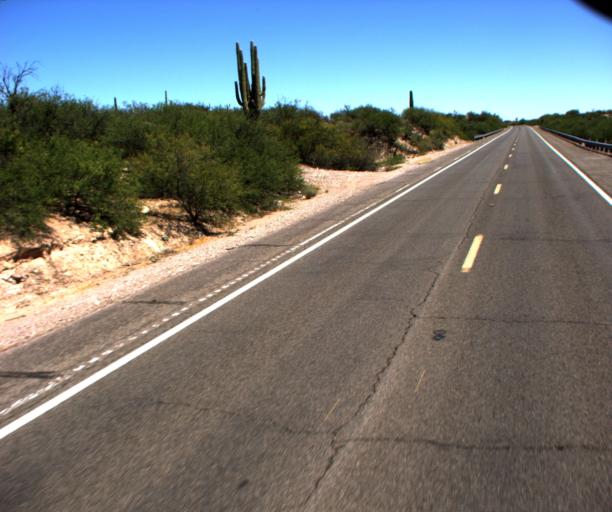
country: US
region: Arizona
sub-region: Pinal County
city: Mammoth
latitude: 32.8253
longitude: -110.6972
